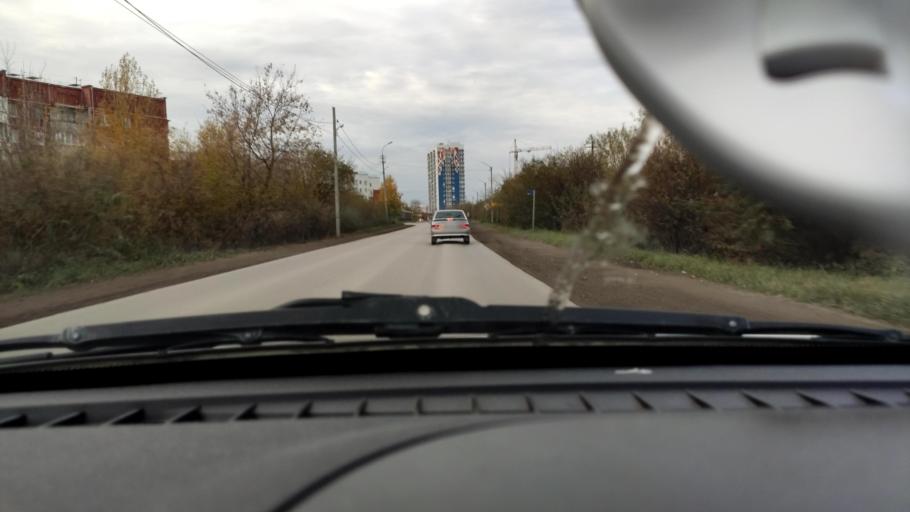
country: RU
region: Perm
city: Kondratovo
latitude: 57.9731
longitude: 56.1120
